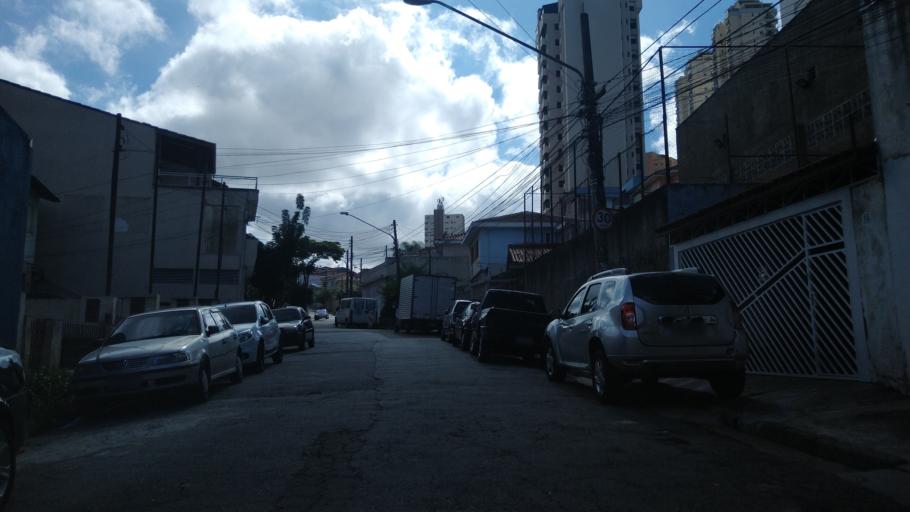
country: BR
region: Sao Paulo
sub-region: Sao Paulo
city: Sao Paulo
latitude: -23.4846
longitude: -46.6270
